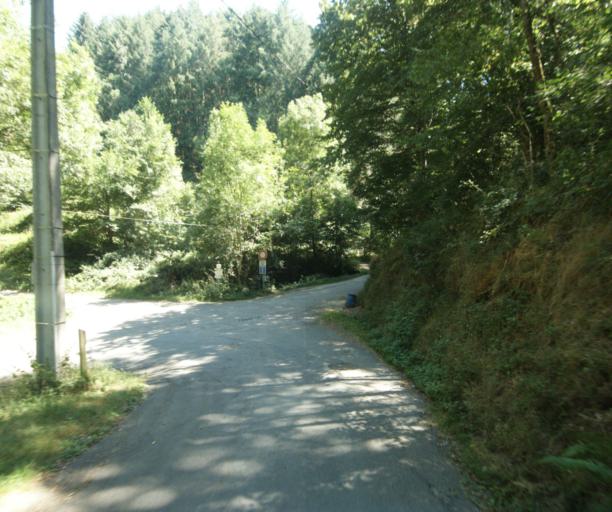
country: FR
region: Rhone-Alpes
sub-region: Departement du Rhone
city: Courzieu
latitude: 45.7380
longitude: 4.5775
